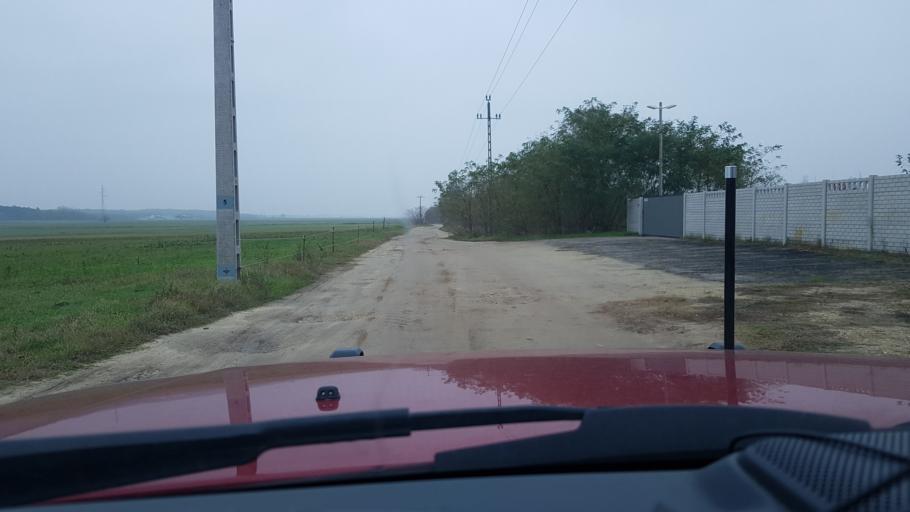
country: HU
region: Pest
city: Felsopakony
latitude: 47.3583
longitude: 19.2566
